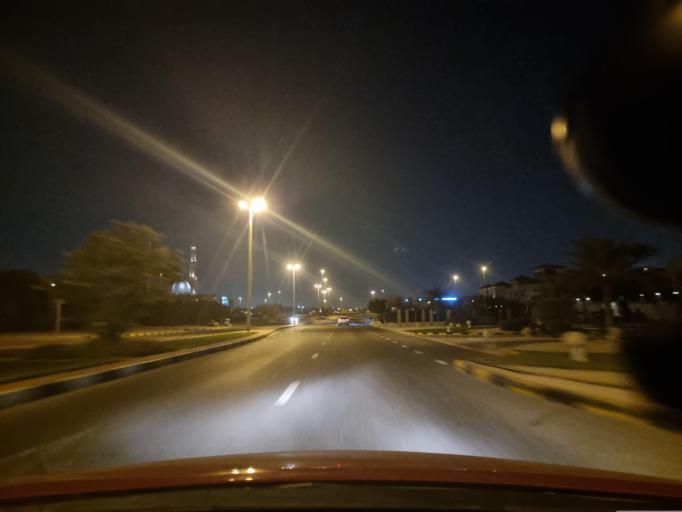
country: AE
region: Ash Shariqah
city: Sharjah
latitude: 25.3448
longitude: 55.4688
